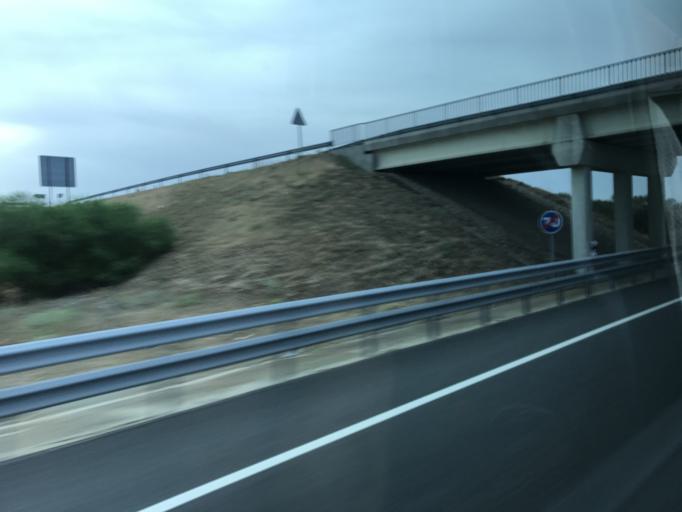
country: ES
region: Castille and Leon
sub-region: Provincia de Segovia
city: San Cristobal de la Vega
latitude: 41.1137
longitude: -4.6383
